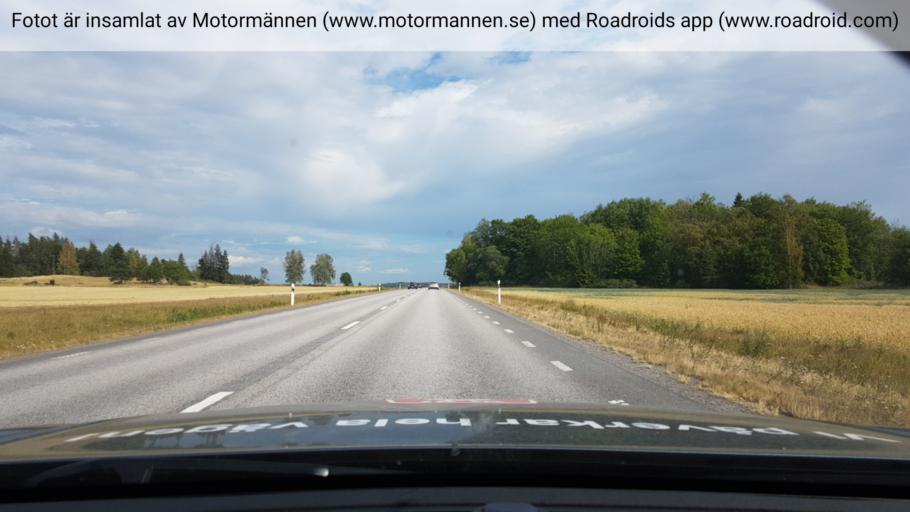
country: SE
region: Uppsala
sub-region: Enkopings Kommun
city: Orsundsbro
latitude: 59.8520
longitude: 17.4483
